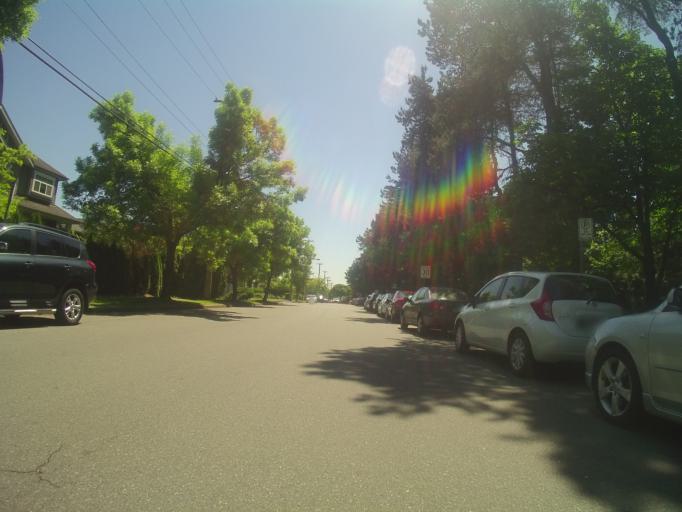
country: CA
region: British Columbia
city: Vancouver
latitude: 49.2208
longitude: -123.1062
